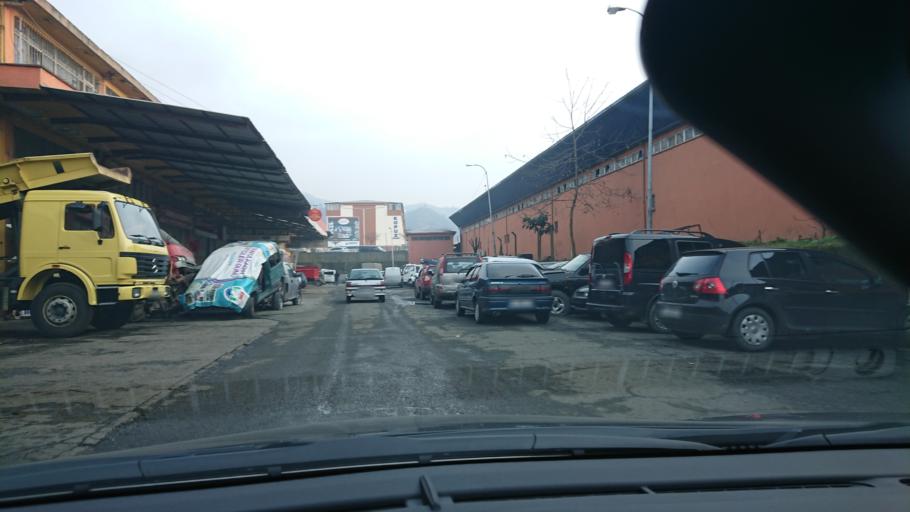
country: TR
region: Rize
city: Gundogdu
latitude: 41.0430
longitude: 40.5762
